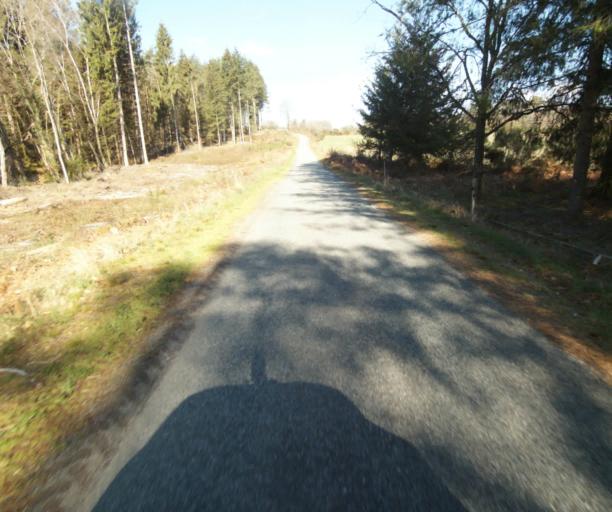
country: FR
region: Limousin
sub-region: Departement de la Correze
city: Correze
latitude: 45.2803
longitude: 1.9158
